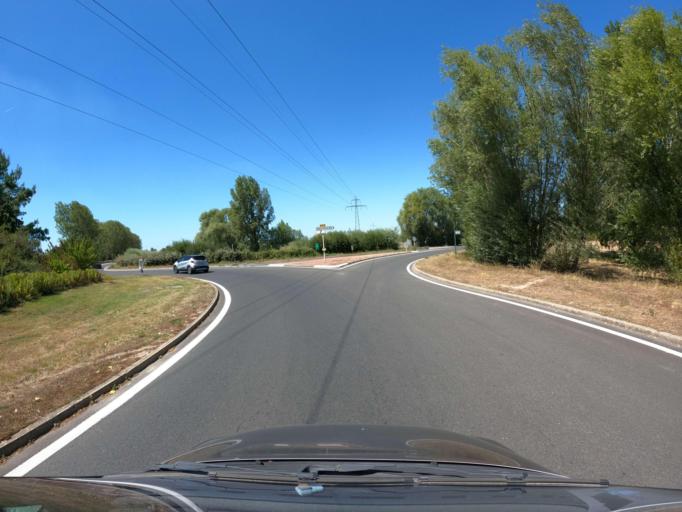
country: FR
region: Pays de la Loire
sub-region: Departement de la Vendee
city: Saint-Jean-de-Monts
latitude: 46.7985
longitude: -2.0548
